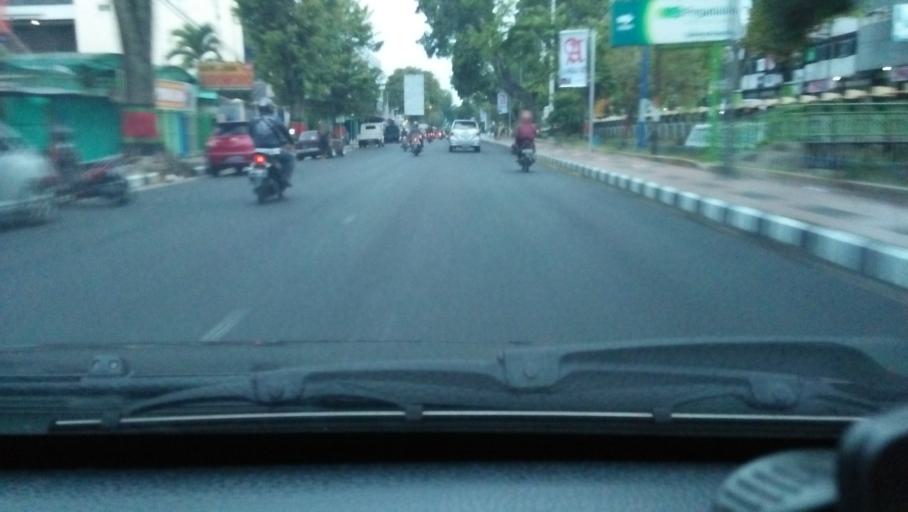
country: ID
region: Central Java
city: Magelang
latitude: -7.4900
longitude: 110.2220
